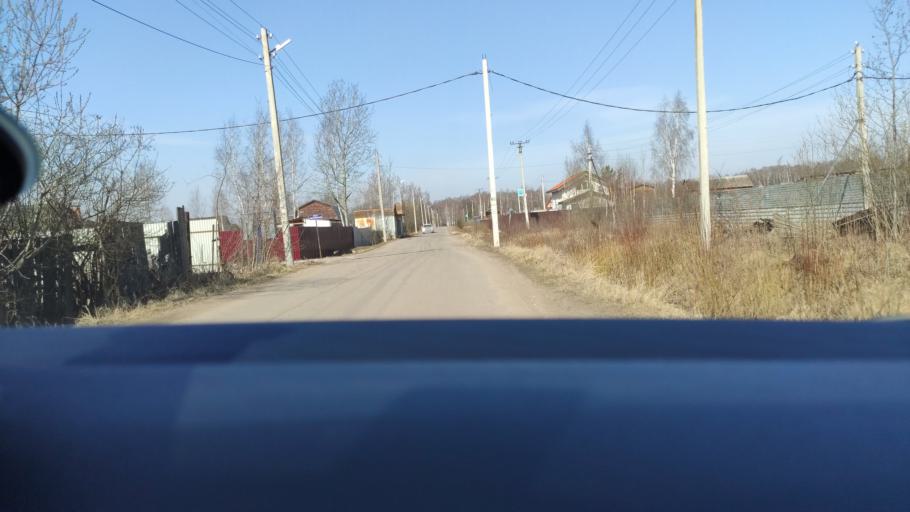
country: RU
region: Moskovskaya
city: Imeni Vorovskogo
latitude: 55.7796
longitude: 38.3680
